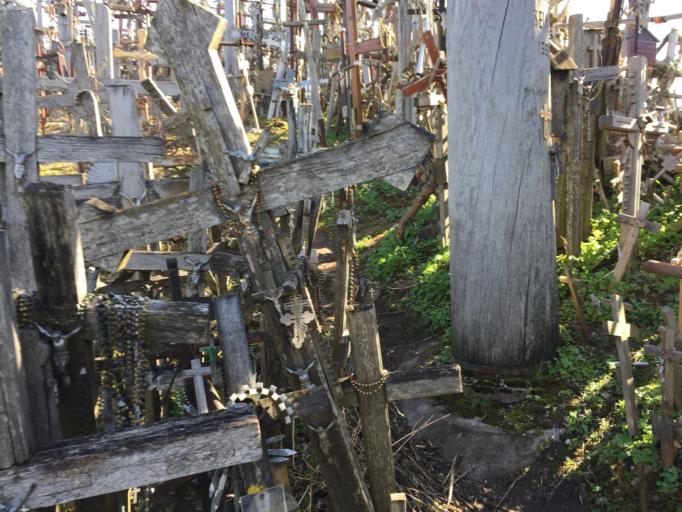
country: LT
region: Siauliu apskritis
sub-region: Siauliai
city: Siauliai
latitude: 56.0153
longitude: 23.4160
